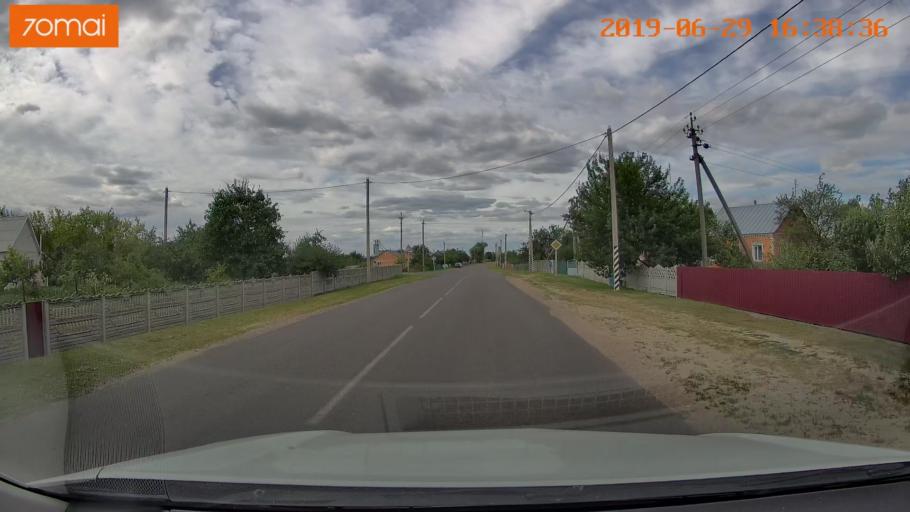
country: BY
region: Brest
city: Luninyets
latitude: 52.2341
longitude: 27.0153
